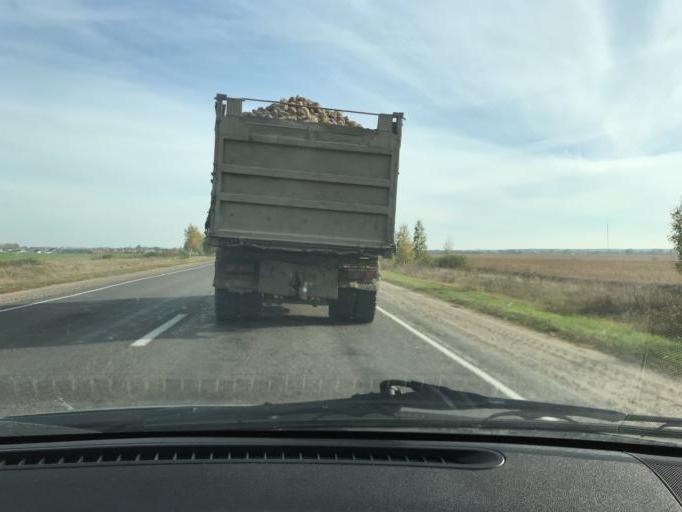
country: BY
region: Brest
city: Asnyezhytsy
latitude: 52.2116
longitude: 26.0464
